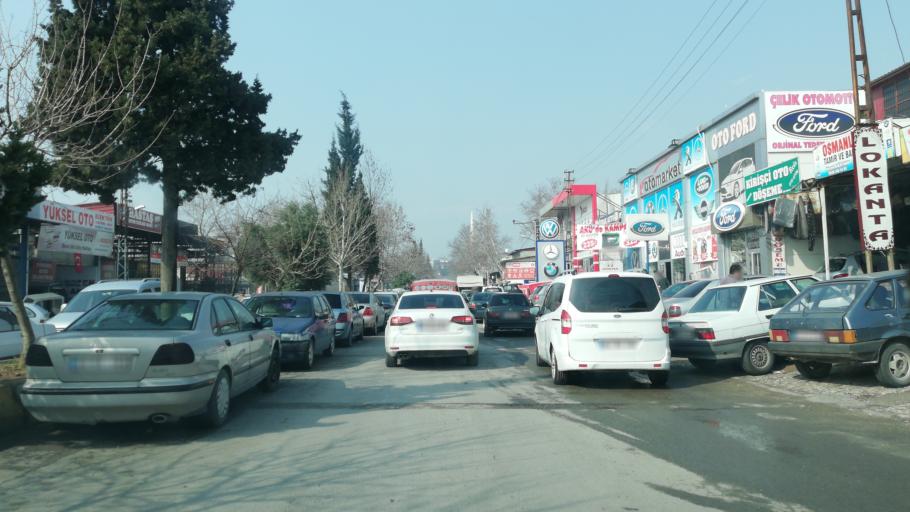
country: TR
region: Kahramanmaras
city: Kahramanmaras
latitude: 37.5624
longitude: 36.9564
